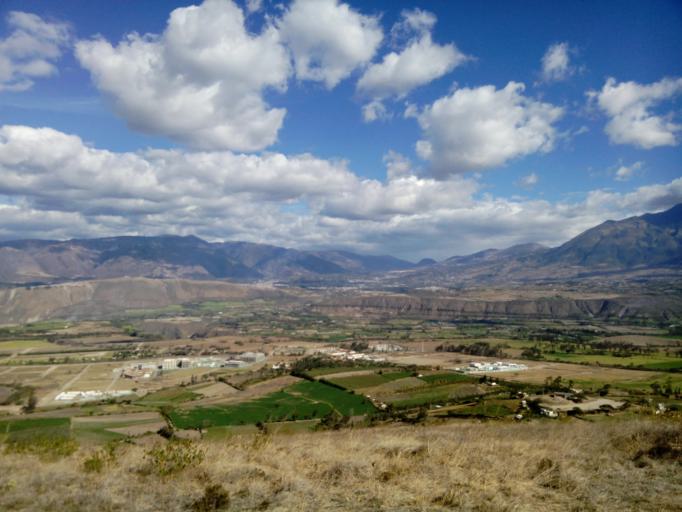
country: EC
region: Imbabura
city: Atuntaqui
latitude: 0.4176
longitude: -78.1844
